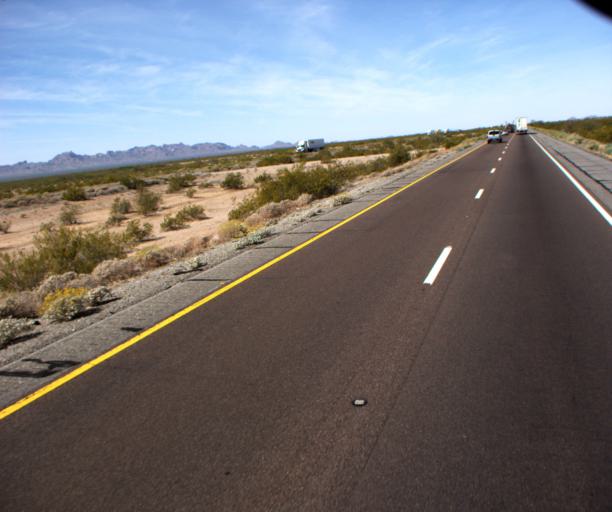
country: US
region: Arizona
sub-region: La Paz County
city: Salome
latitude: 33.5530
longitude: -113.2457
